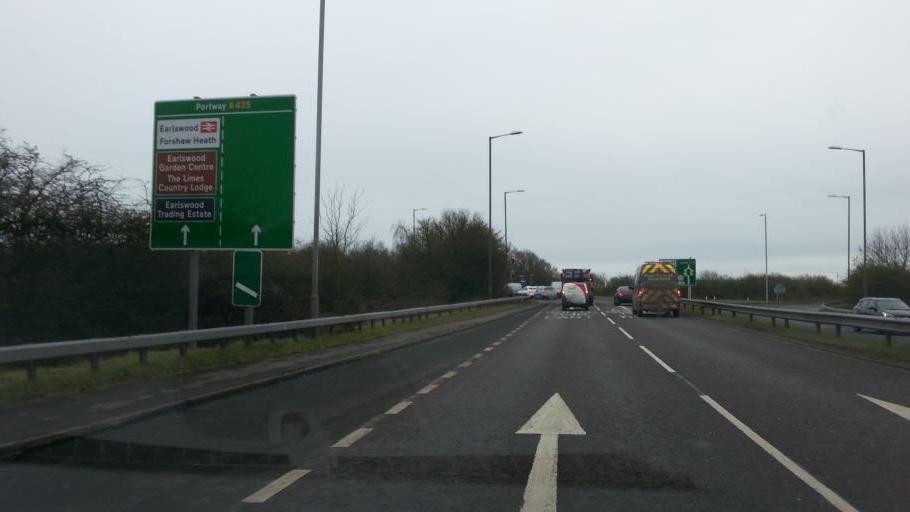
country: GB
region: England
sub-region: Solihull
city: Tidbury Green
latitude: 52.3569
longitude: -1.8870
